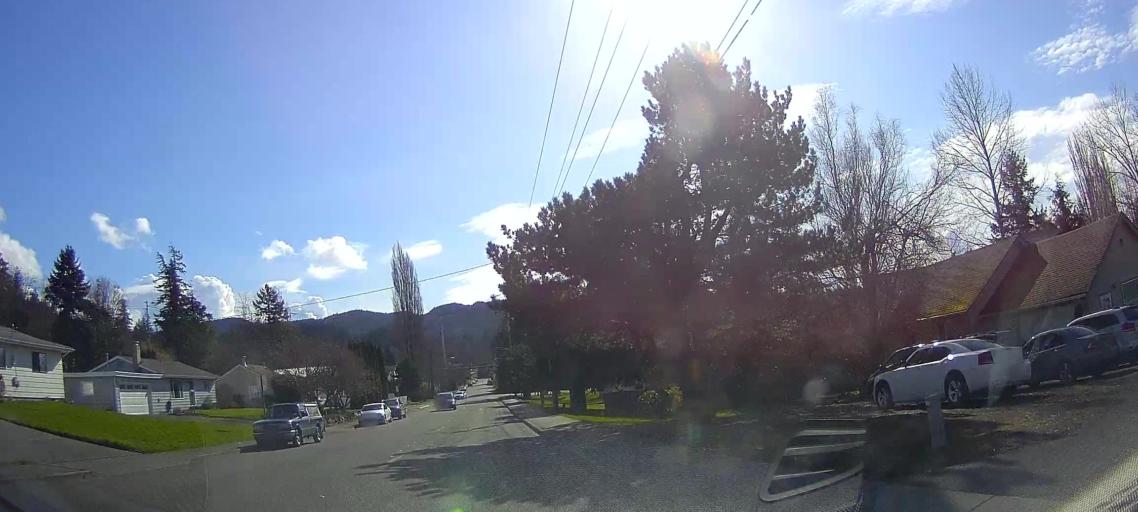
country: US
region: Washington
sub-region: Whatcom County
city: Bellingham
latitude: 48.7187
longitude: -122.4755
